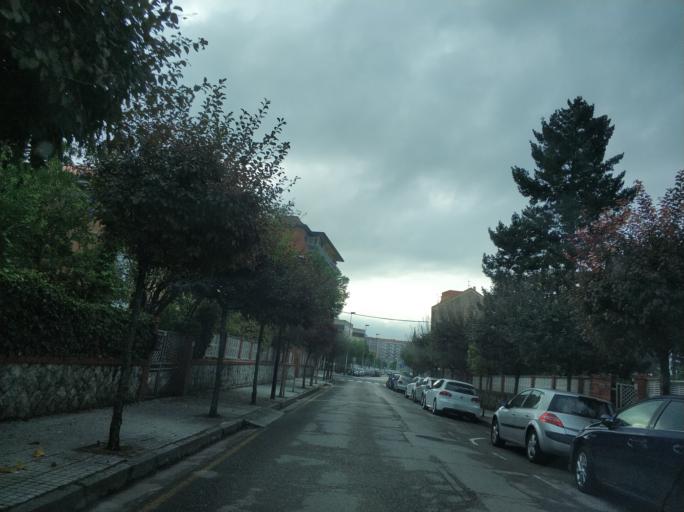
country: ES
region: Cantabria
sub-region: Provincia de Cantabria
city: Torrelavega
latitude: 43.3539
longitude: -4.0550
